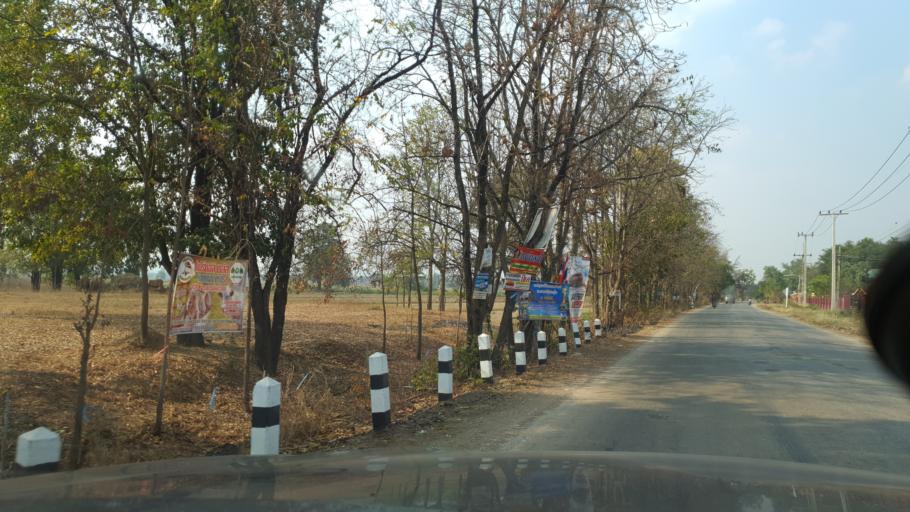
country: TH
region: Sukhothai
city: Ban Dan Lan Hoi
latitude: 17.1047
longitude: 99.5517
